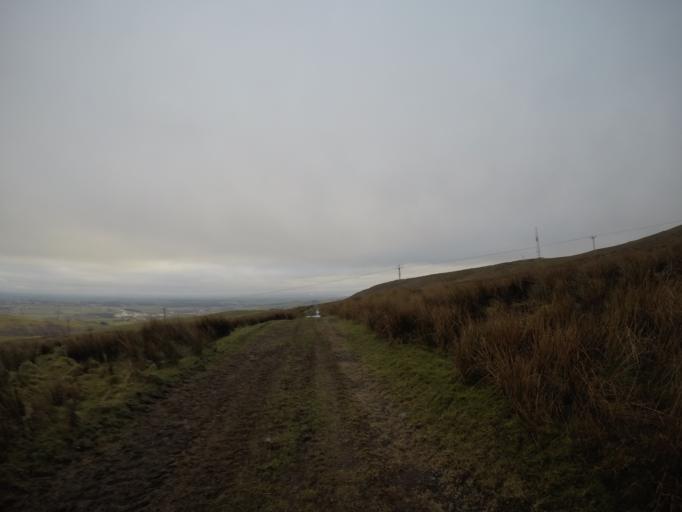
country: GB
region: Scotland
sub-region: North Ayrshire
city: Dalry
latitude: 55.7341
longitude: -4.7678
